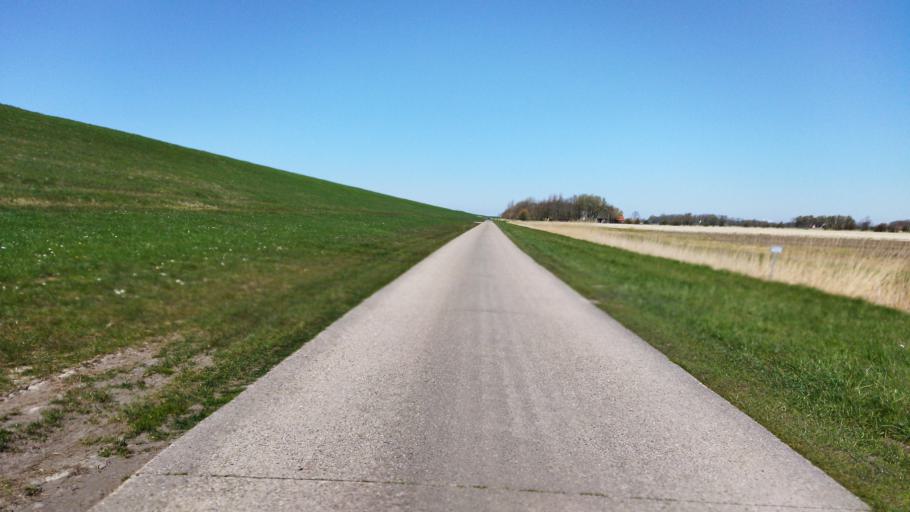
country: DE
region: Lower Saxony
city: Misselwarden
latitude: 53.6780
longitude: 8.4854
